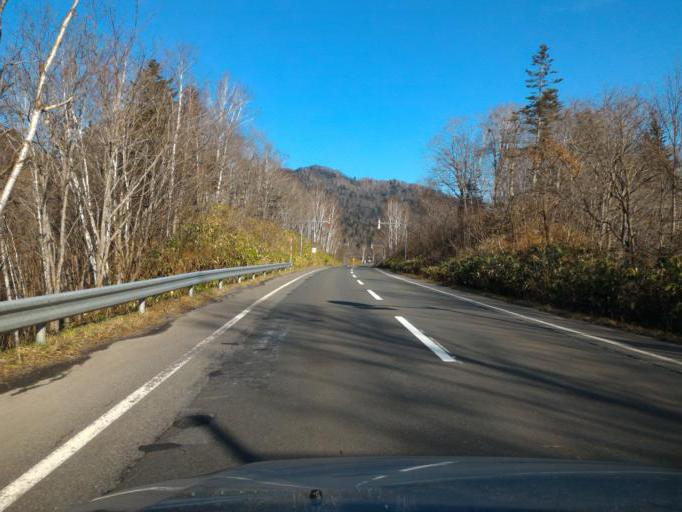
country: JP
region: Hokkaido
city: Ashibetsu
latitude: 43.2996
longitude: 142.1128
